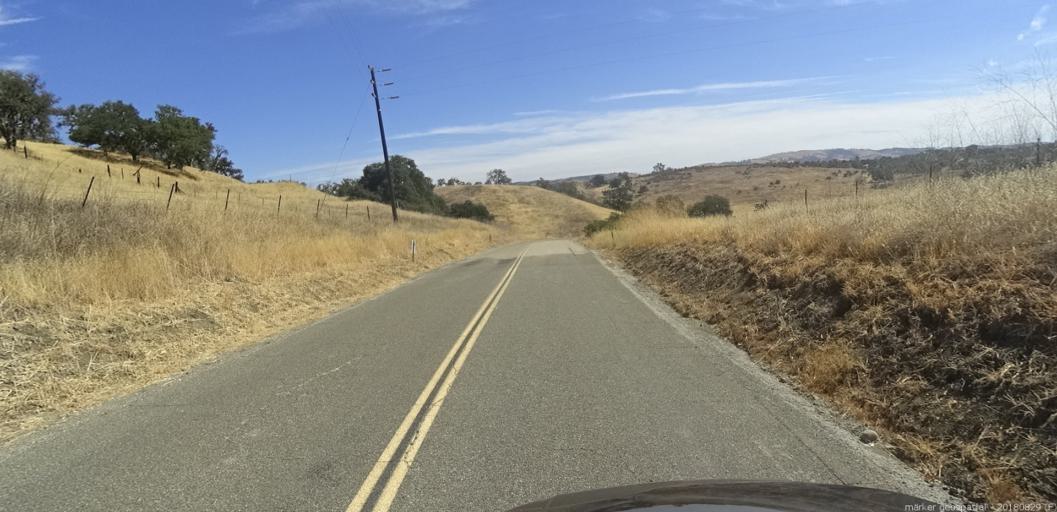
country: US
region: California
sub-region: San Luis Obispo County
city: Lake Nacimiento
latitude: 35.8278
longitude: -120.9800
